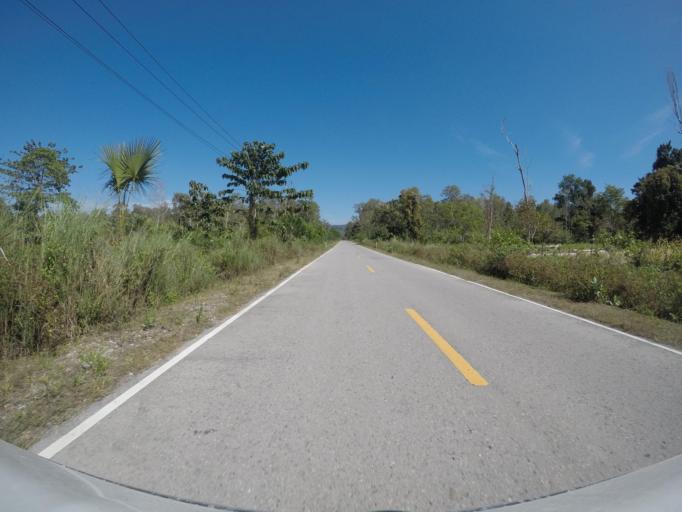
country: TL
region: Viqueque
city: Viqueque
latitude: -8.9639
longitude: 126.0185
